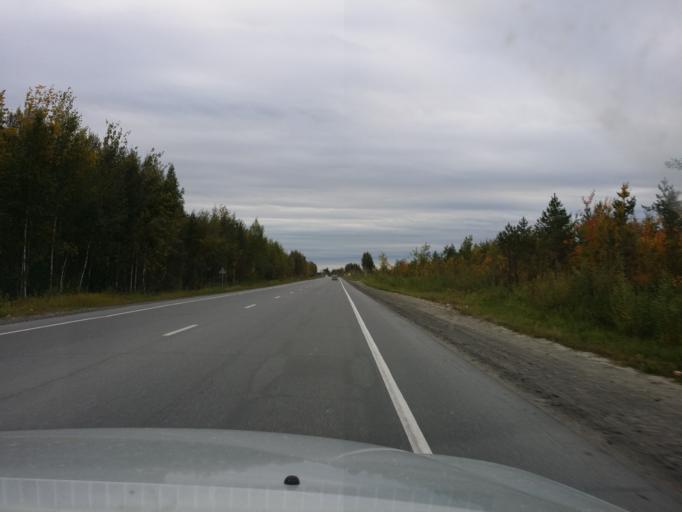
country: RU
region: Khanty-Mansiyskiy Avtonomnyy Okrug
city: Megion
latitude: 61.0661
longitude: 76.2602
